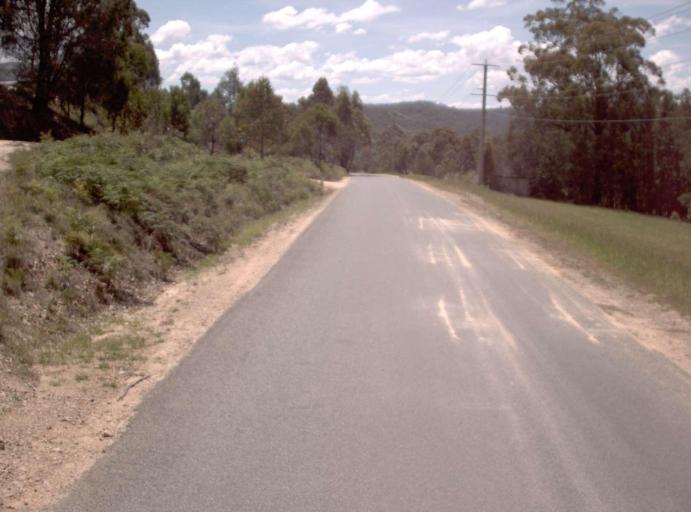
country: AU
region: New South Wales
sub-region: Bombala
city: Bombala
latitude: -37.5499
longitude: 148.9371
